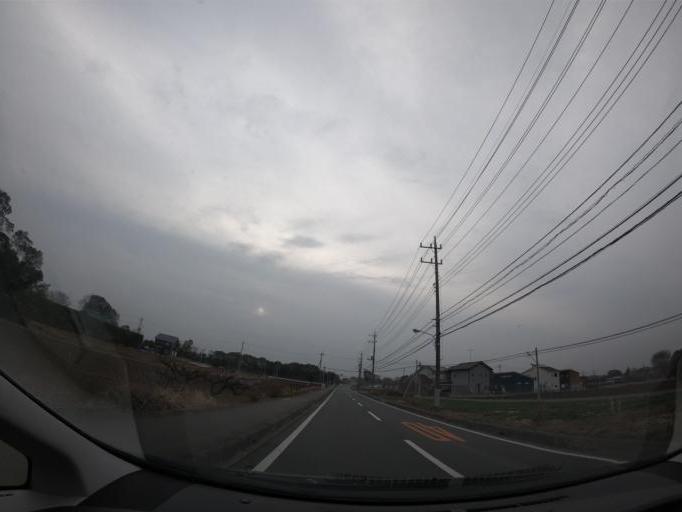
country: JP
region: Ibaraki
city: Moriya
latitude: 35.9566
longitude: 139.9732
